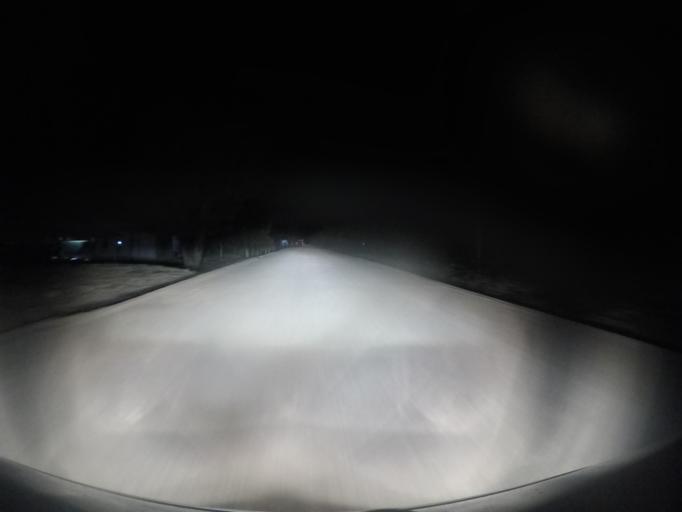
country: TL
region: Viqueque
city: Viqueque
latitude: -8.8124
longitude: 126.5379
